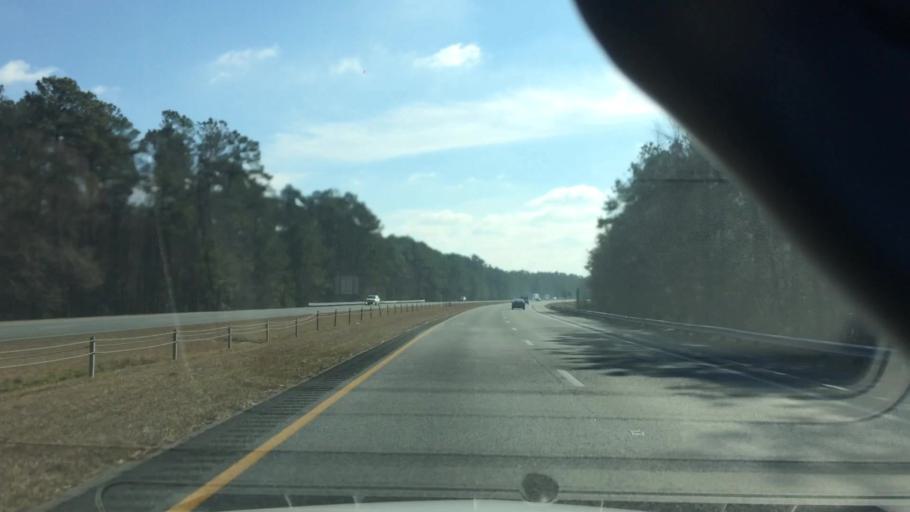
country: US
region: North Carolina
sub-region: Duplin County
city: Wallace
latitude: 34.7473
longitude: -77.9454
